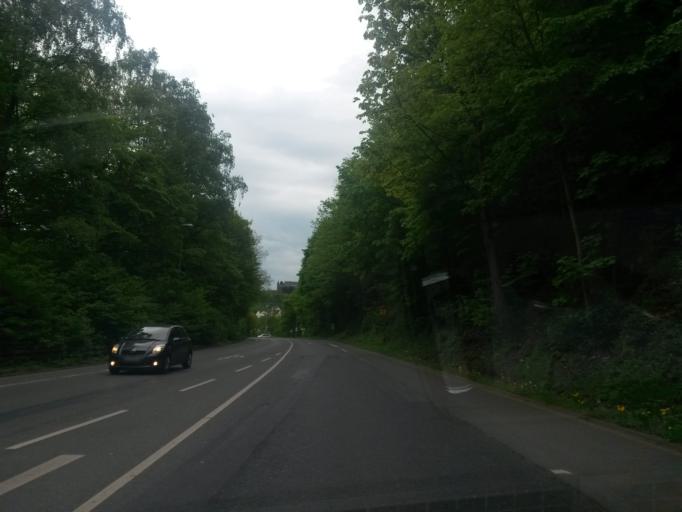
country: DE
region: North Rhine-Westphalia
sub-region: Regierungsbezirk Arnsberg
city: Nachrodt-Wiblingwerde
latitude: 51.3531
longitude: 7.5592
